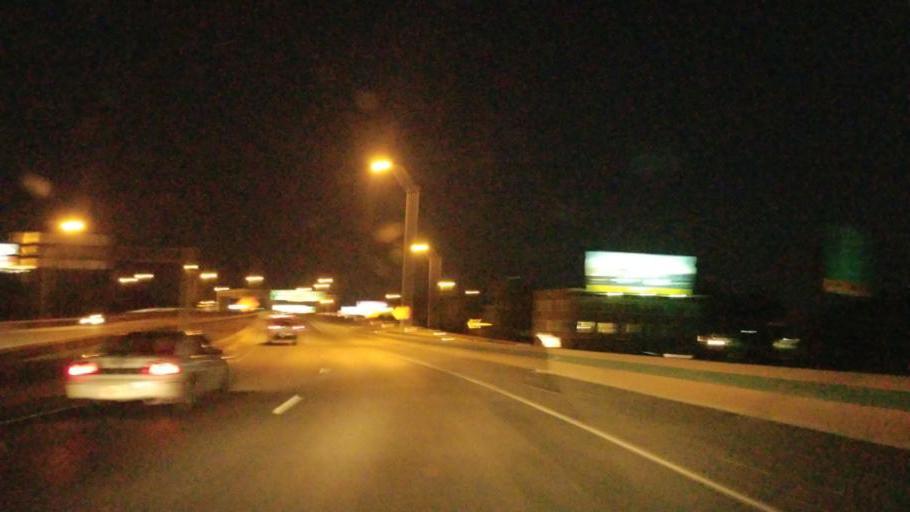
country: US
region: Texas
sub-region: Potter County
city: Amarillo
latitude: 35.2001
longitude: -101.8357
